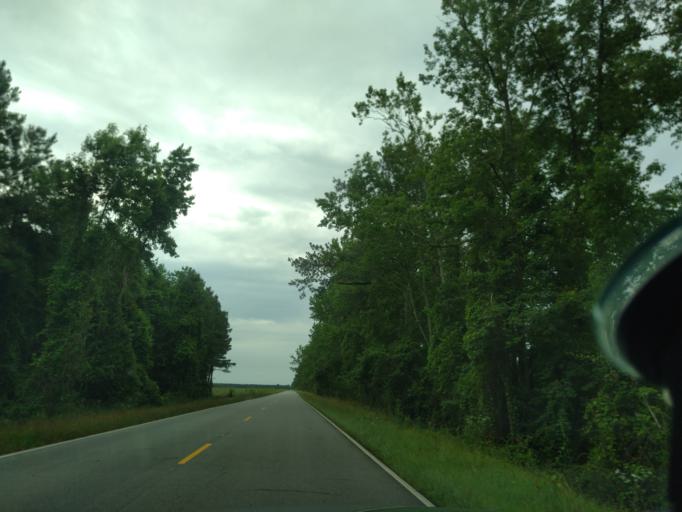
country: US
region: North Carolina
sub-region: Washington County
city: Plymouth
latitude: 35.8701
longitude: -76.5926
